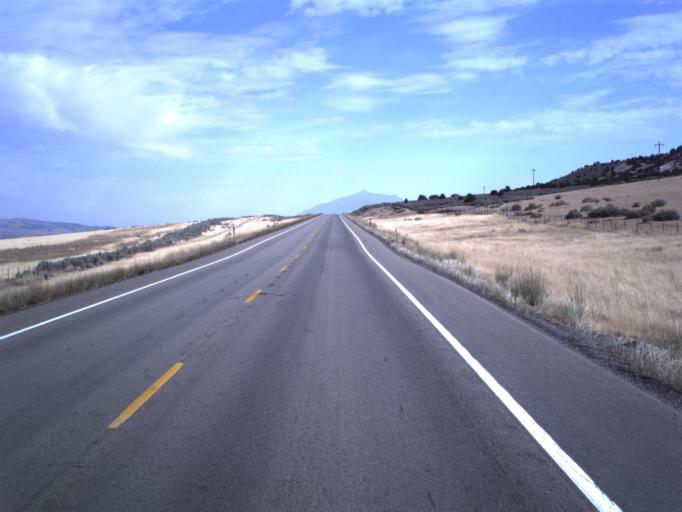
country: US
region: Utah
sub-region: Sanpete County
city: Gunnison
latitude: 39.4104
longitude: -111.9256
